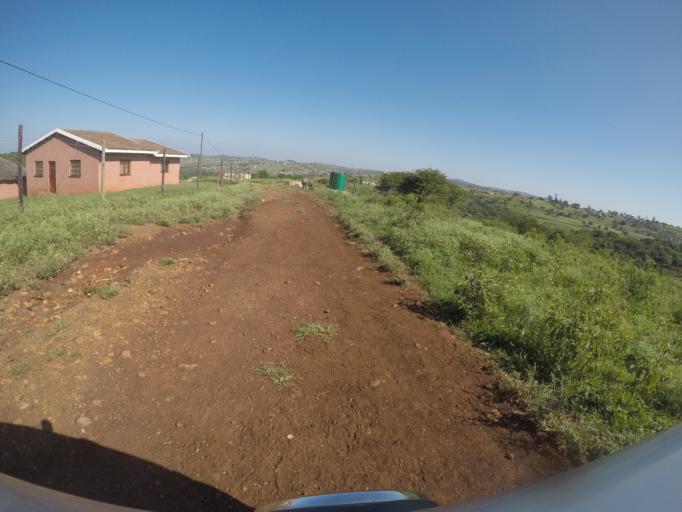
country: ZA
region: KwaZulu-Natal
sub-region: uThungulu District Municipality
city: Empangeni
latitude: -28.5741
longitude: 31.7316
